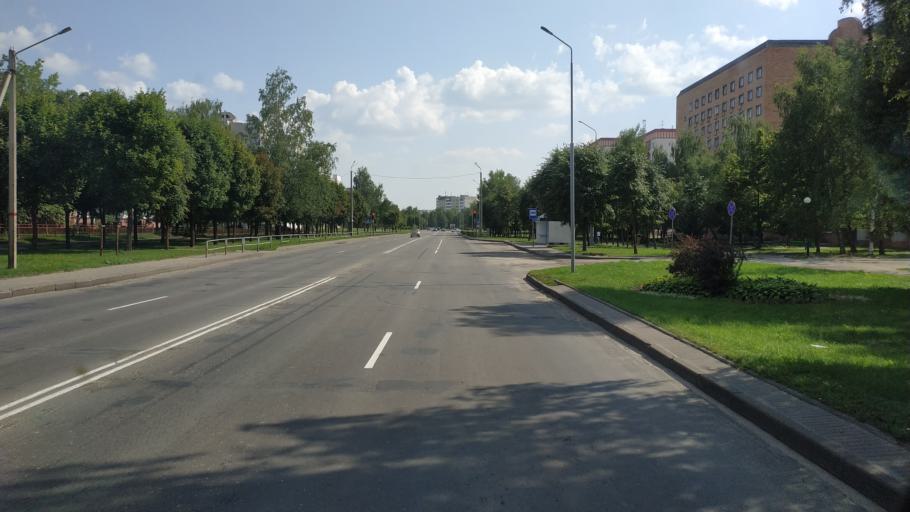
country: BY
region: Mogilev
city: Buynichy
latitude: 53.8720
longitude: 30.3129
